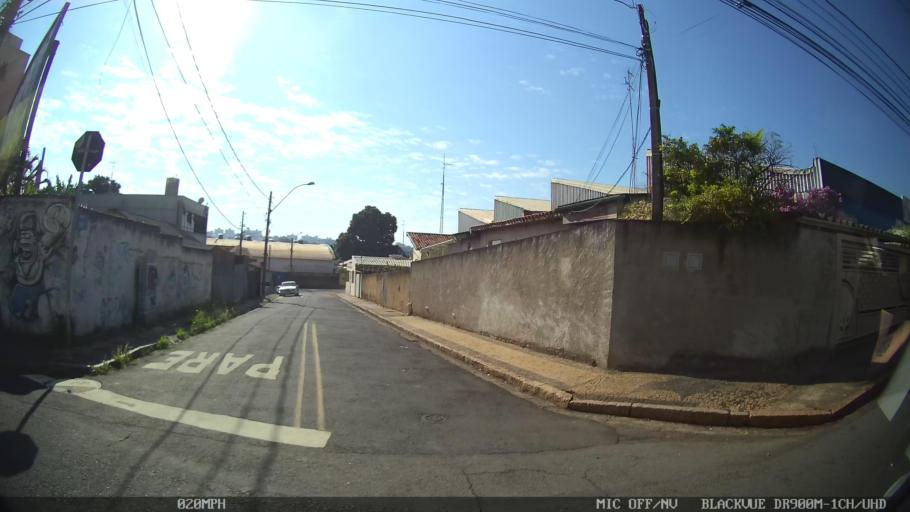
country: BR
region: Sao Paulo
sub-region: Americana
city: Americana
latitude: -22.7448
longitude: -47.3268
